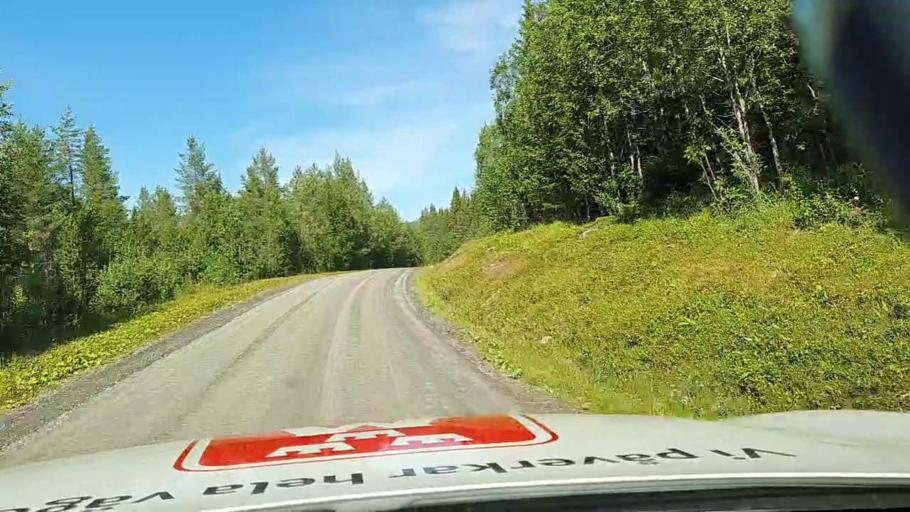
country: SE
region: Jaemtland
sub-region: Krokoms Kommun
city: Valla
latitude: 64.1033
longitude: 14.1502
